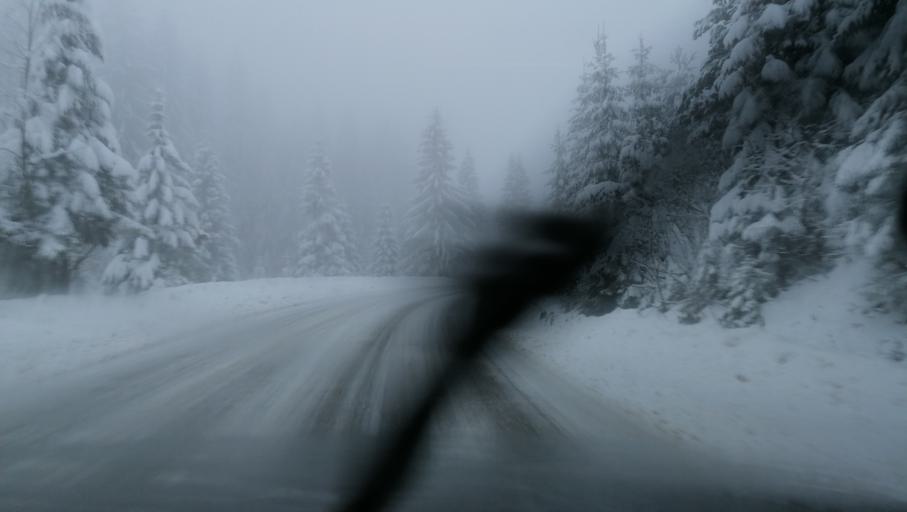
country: BA
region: Republika Srpska
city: Han Pijesak
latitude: 44.1225
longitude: 18.9656
